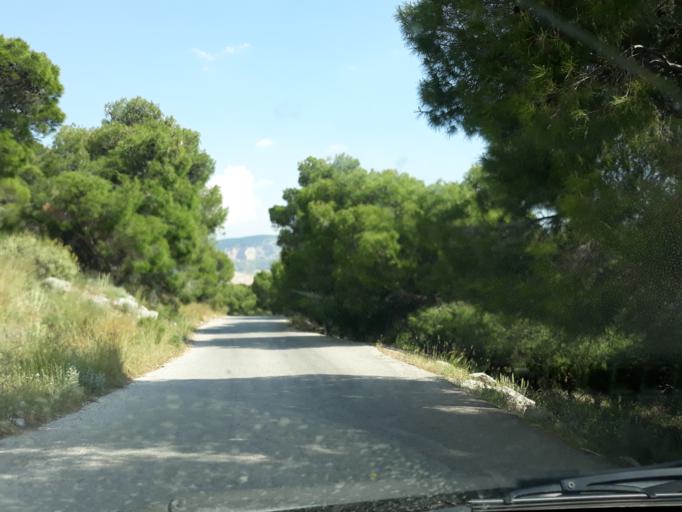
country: GR
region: Attica
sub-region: Nomarchia Dytikis Attikis
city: Fyli
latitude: 38.0948
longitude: 23.6336
